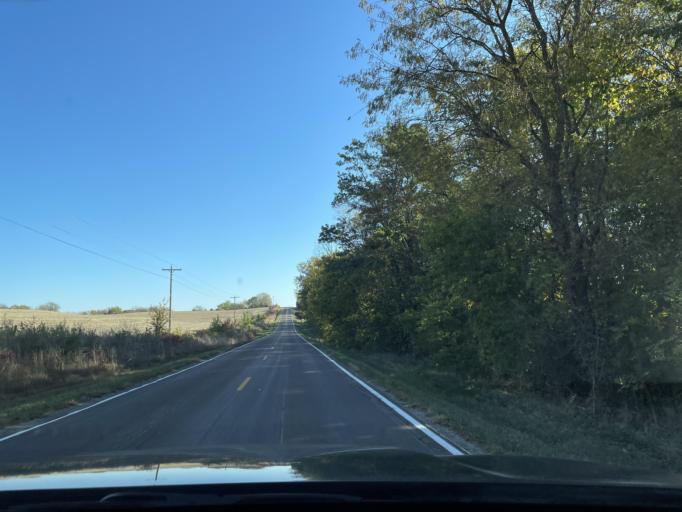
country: US
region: Missouri
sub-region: Andrew County
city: Savannah
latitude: 39.9184
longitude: -94.8709
